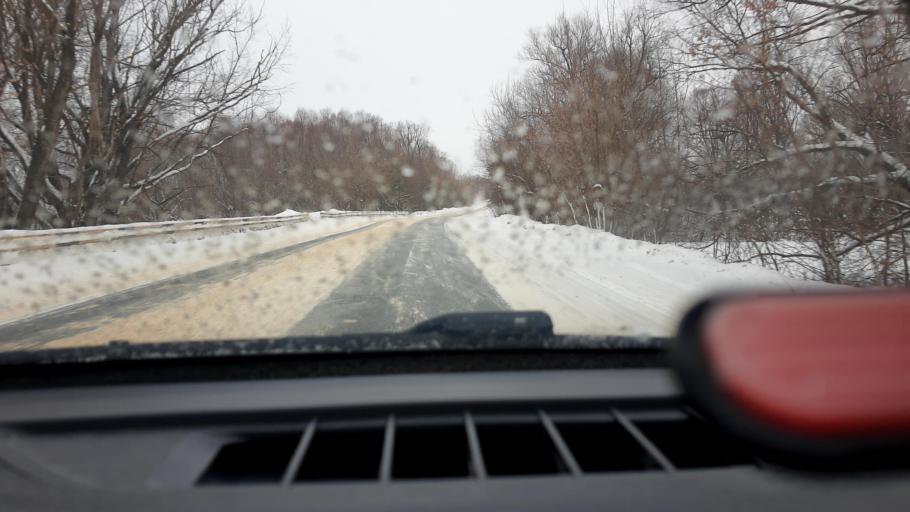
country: RU
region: Nizjnij Novgorod
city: Buturlino
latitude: 55.5730
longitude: 44.9071
